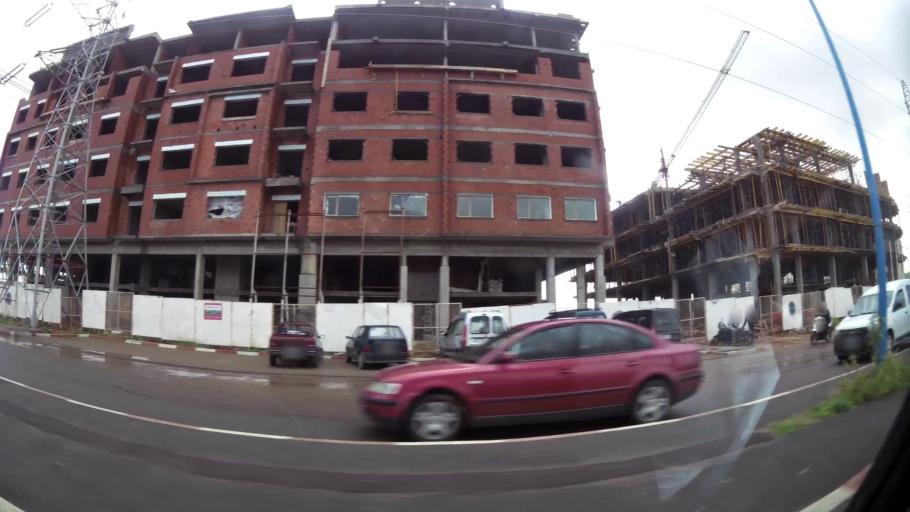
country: MA
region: Grand Casablanca
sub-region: Mediouna
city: Tit Mellil
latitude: 33.5906
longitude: -7.5275
